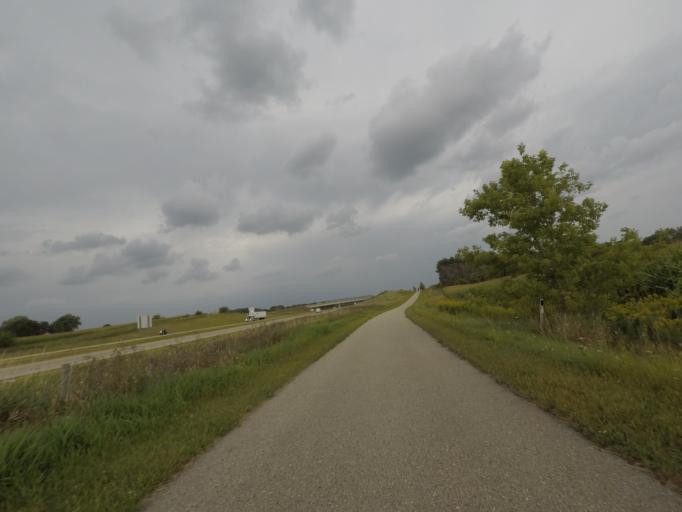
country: US
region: Wisconsin
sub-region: Jefferson County
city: Jefferson
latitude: 42.9826
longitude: -88.8269
